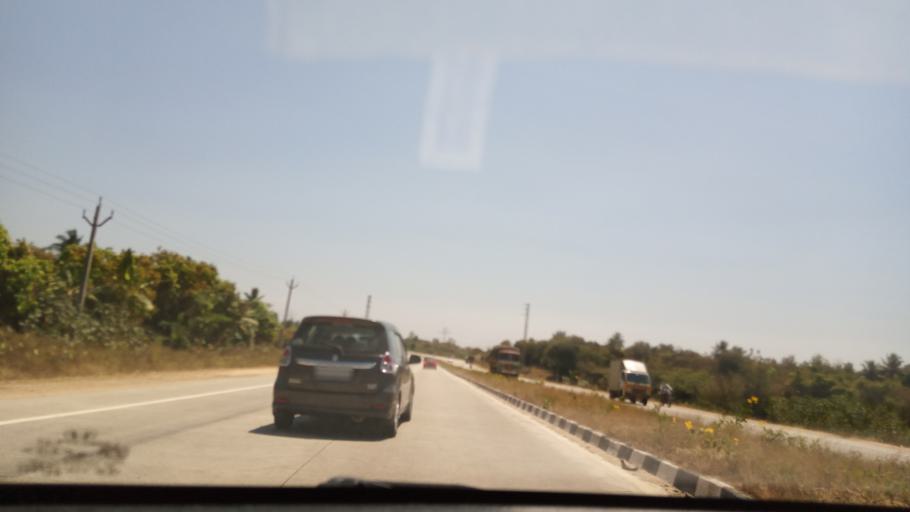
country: IN
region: Andhra Pradesh
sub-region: Chittoor
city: Chittoor
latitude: 13.1996
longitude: 78.9718
